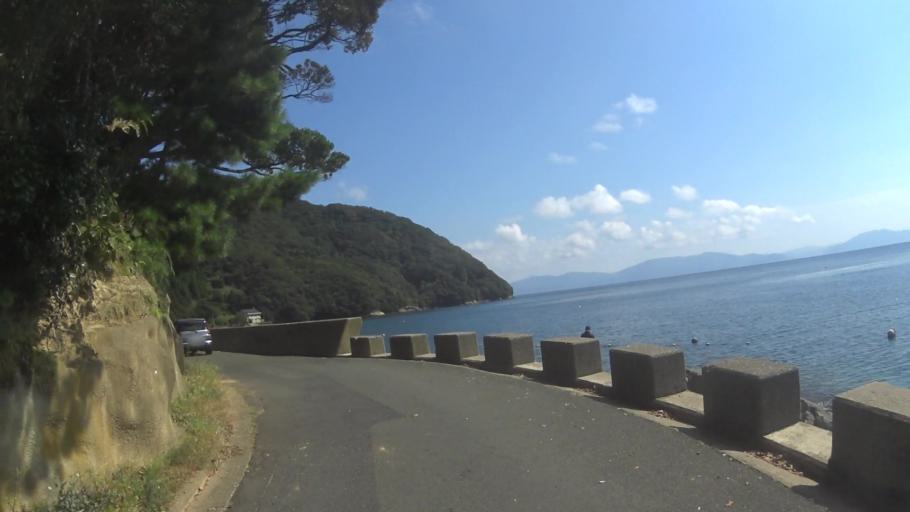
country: JP
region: Kyoto
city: Miyazu
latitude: 35.6646
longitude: 135.2878
